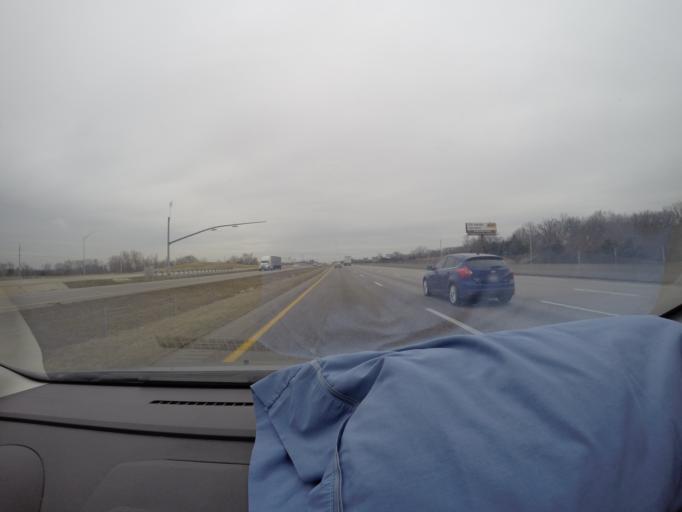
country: US
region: Missouri
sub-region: Saint Charles County
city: Wentzville
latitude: 38.8116
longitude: -90.9350
